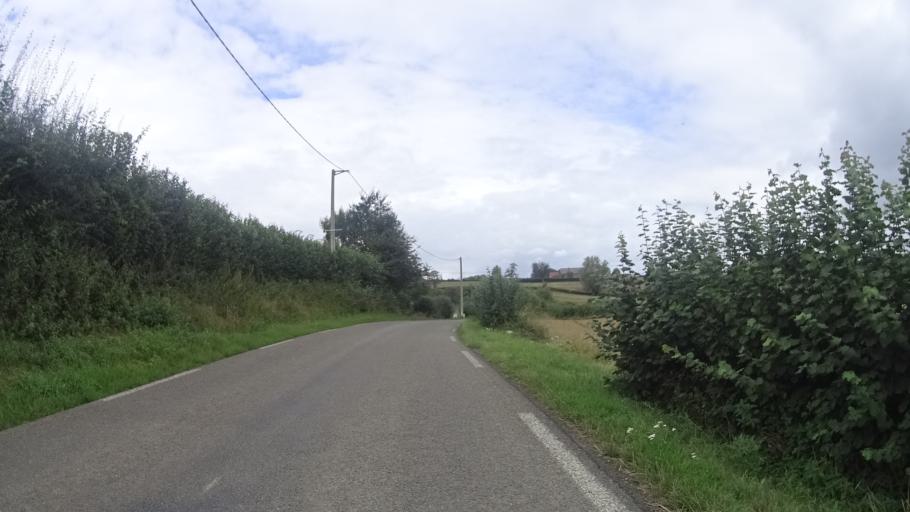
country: FR
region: Nord-Pas-de-Calais
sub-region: Departement du Nord
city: Berlaimont
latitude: 50.1869
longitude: 3.8074
